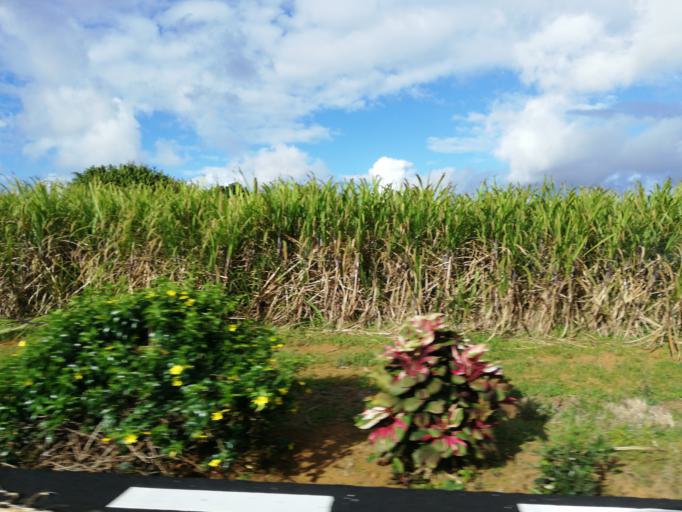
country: MU
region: Flacq
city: Sebastopol
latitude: -20.3056
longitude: 57.6927
